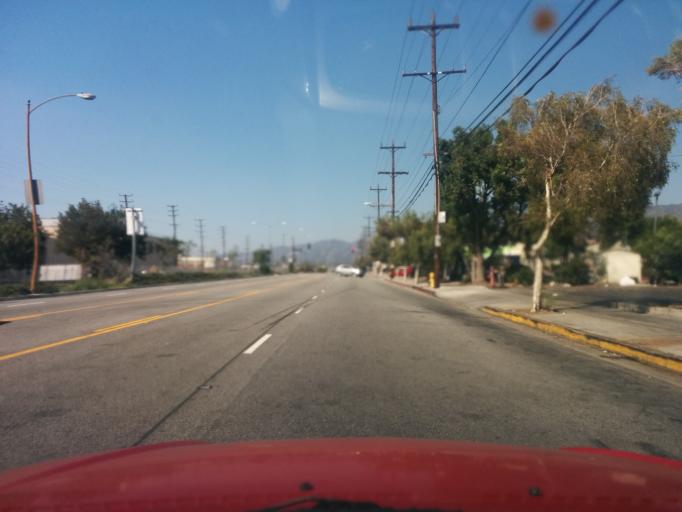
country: US
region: California
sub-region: Los Angeles County
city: Glendale
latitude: 34.1431
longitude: -118.2699
